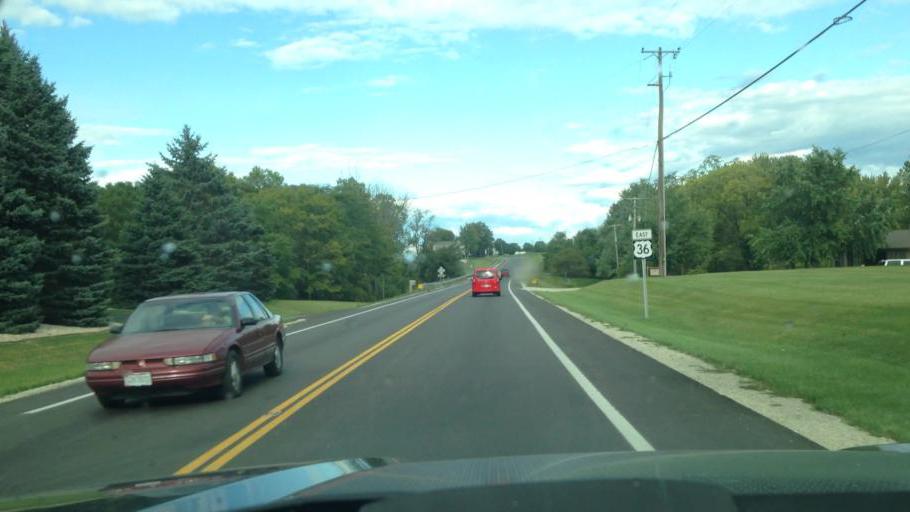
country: US
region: Ohio
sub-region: Darke County
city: Greenville
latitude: 40.1004
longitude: -84.5990
